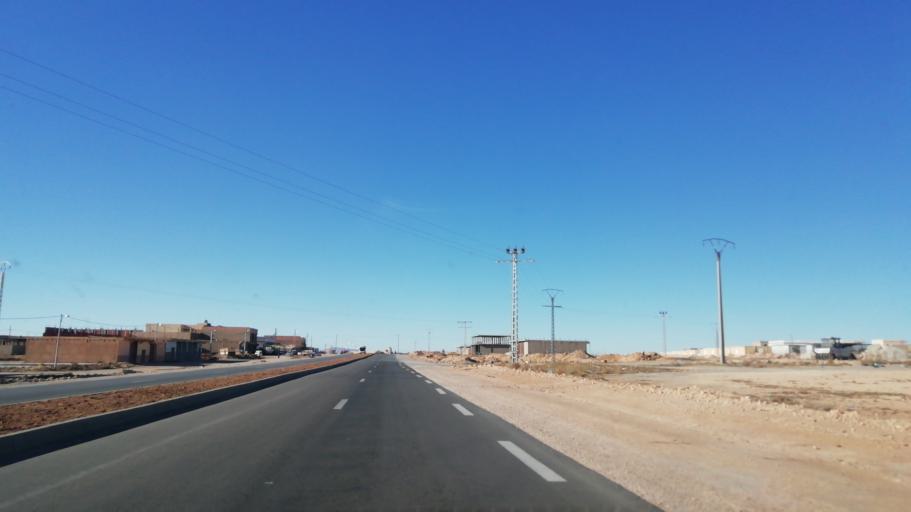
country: DZ
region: Tlemcen
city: Sebdou
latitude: 34.2185
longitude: -1.2477
